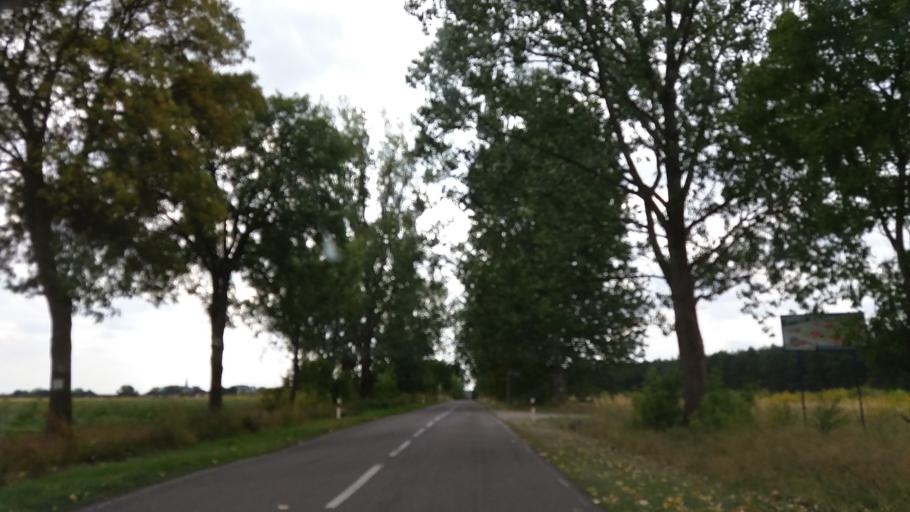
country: PL
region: West Pomeranian Voivodeship
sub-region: Powiat stargardzki
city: Kobylanka
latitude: 53.3332
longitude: 14.8594
